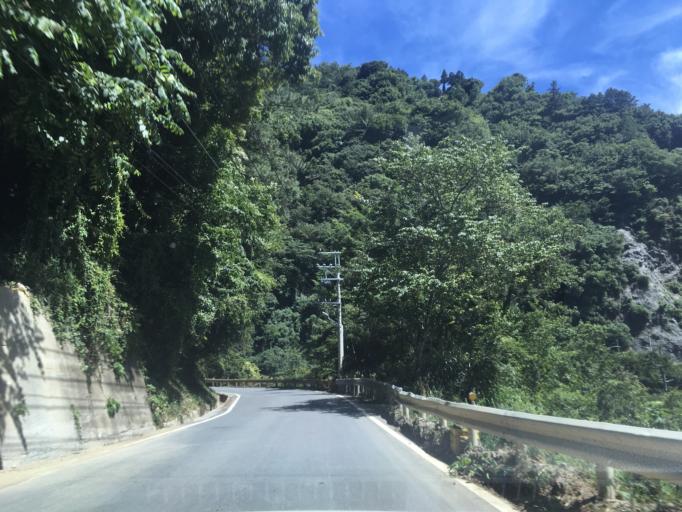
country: TW
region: Taiwan
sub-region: Nantou
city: Puli
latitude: 24.2385
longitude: 121.2529
